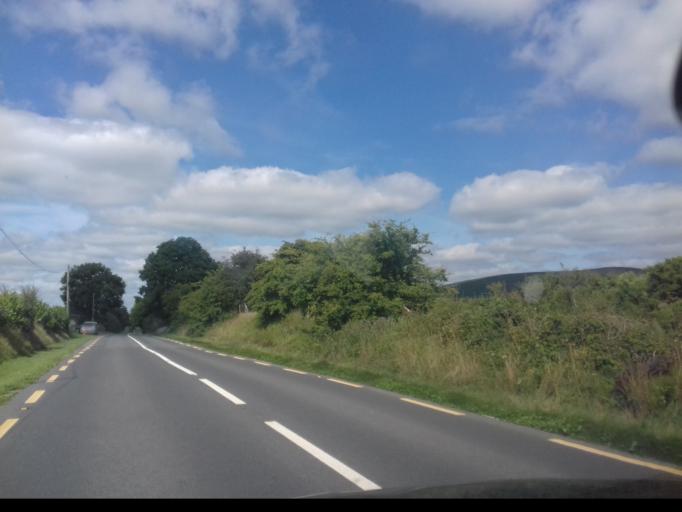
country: IE
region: Leinster
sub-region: Wicklow
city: Valleymount
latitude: 53.0680
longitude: -6.6182
